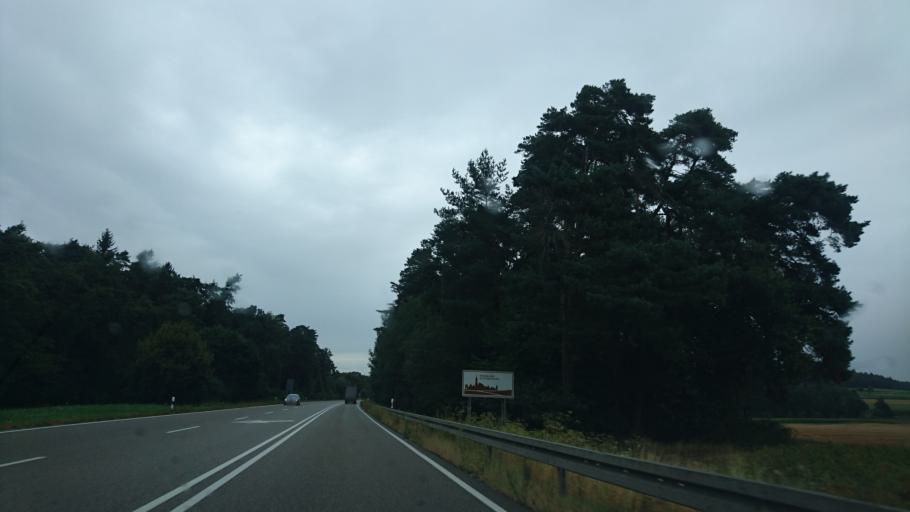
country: DE
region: Bavaria
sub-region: Upper Bavaria
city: Gachenbach
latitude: 48.5108
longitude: 11.2215
